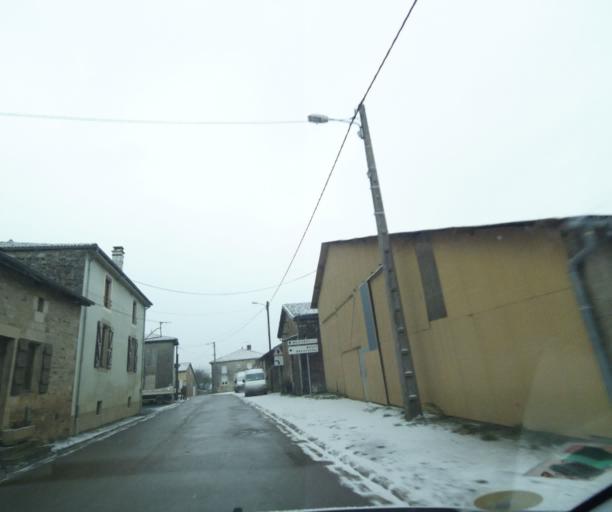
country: FR
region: Champagne-Ardenne
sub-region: Departement de la Haute-Marne
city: Wassy
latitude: 48.4741
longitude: 5.0357
